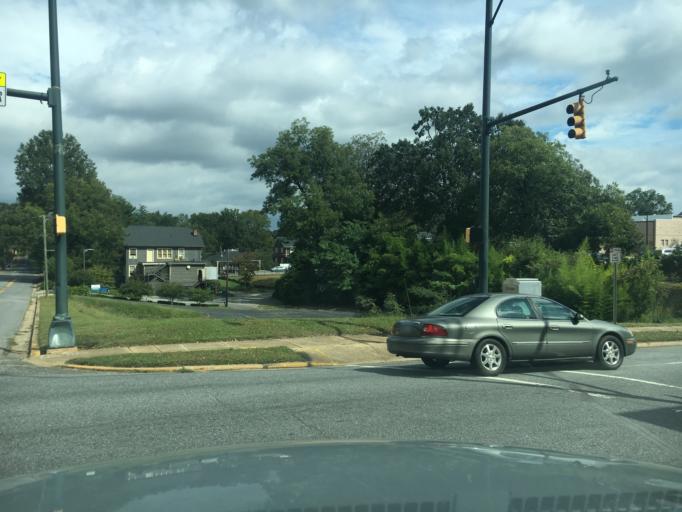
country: US
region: North Carolina
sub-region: Catawba County
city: Hickory
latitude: 35.7344
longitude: -81.3422
